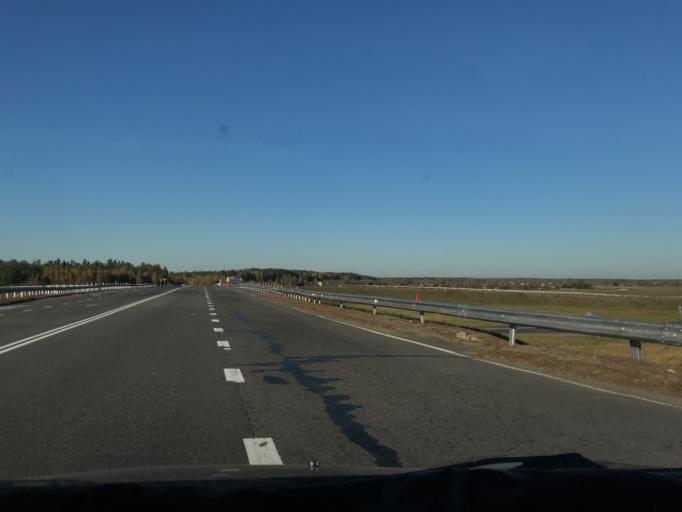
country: BY
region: Gomel
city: Kalinkavichy
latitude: 52.1248
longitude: 29.3765
